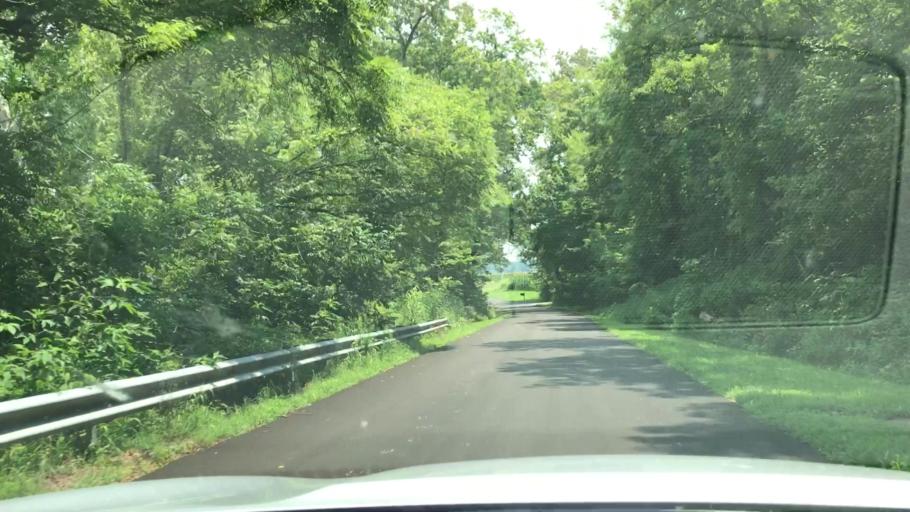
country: US
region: Kentucky
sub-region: Todd County
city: Elkton
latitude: 36.7786
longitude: -87.1486
